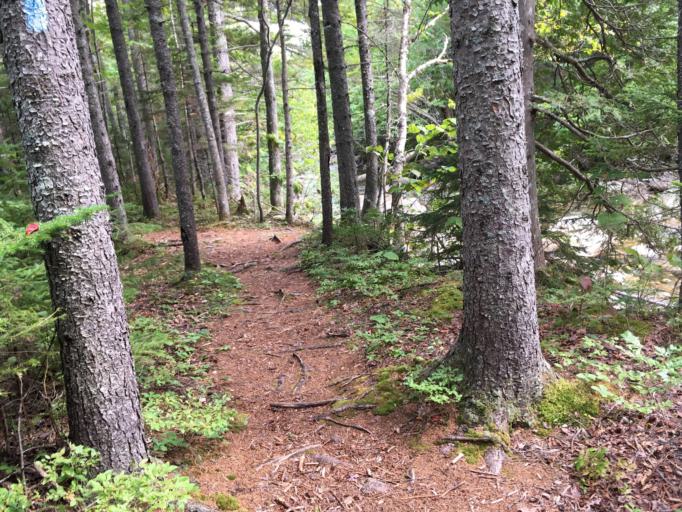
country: US
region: Maine
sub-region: Penobscot County
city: Millinocket
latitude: 45.9207
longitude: -68.8573
